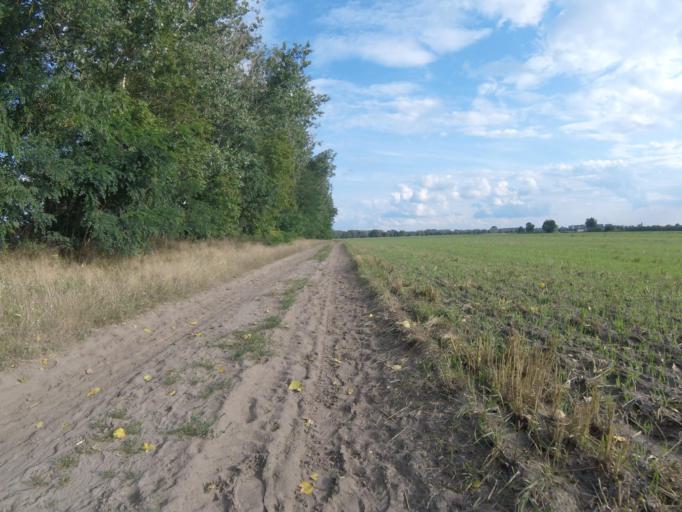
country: DE
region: Brandenburg
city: Mittenwalde
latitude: 52.2849
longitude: 13.5530
